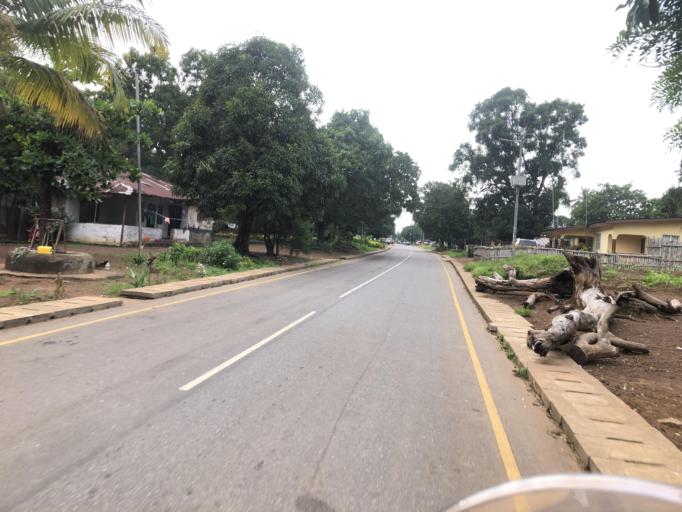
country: SL
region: Northern Province
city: Port Loko
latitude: 8.7707
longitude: -12.7910
